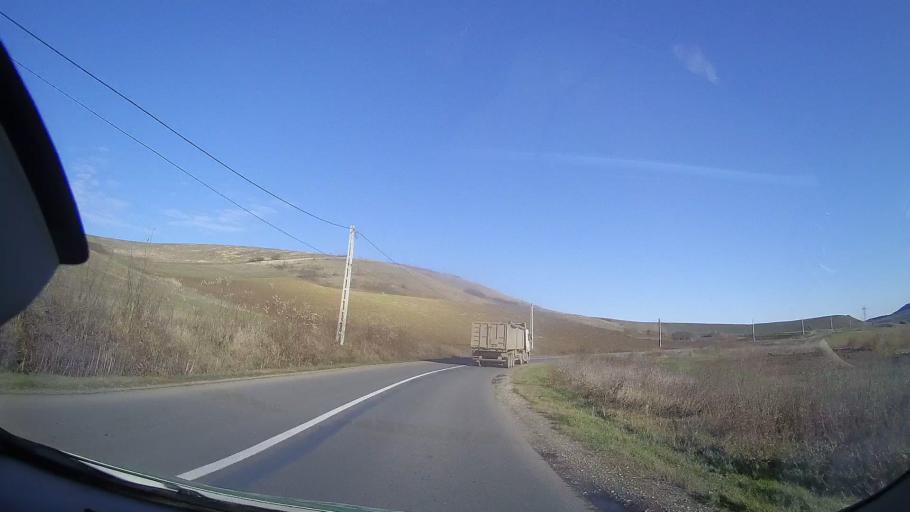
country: RO
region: Mures
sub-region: Comuna Mihesu de Campie
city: Mihesu de Campie
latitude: 46.6505
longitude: 24.1558
